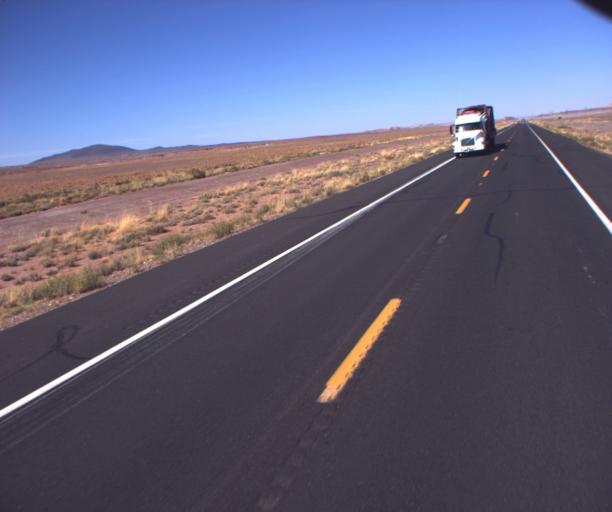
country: US
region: Arizona
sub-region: Coconino County
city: Tuba City
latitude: 35.9064
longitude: -111.4046
